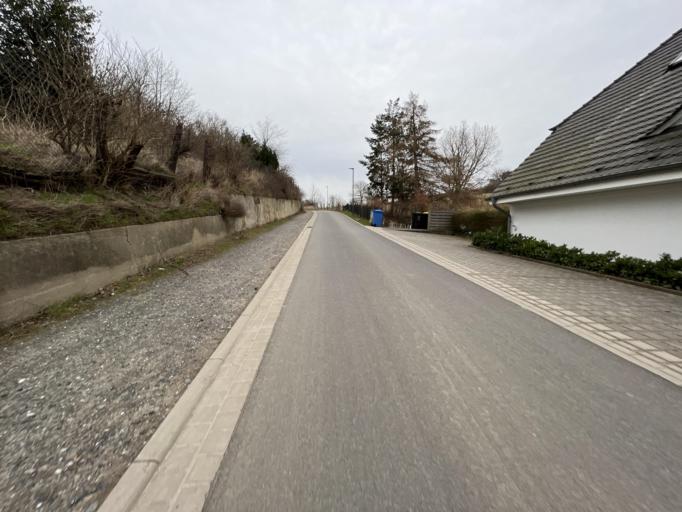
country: DE
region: Mecklenburg-Vorpommern
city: Ostseebad Gohren
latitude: 54.3395
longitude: 13.7429
